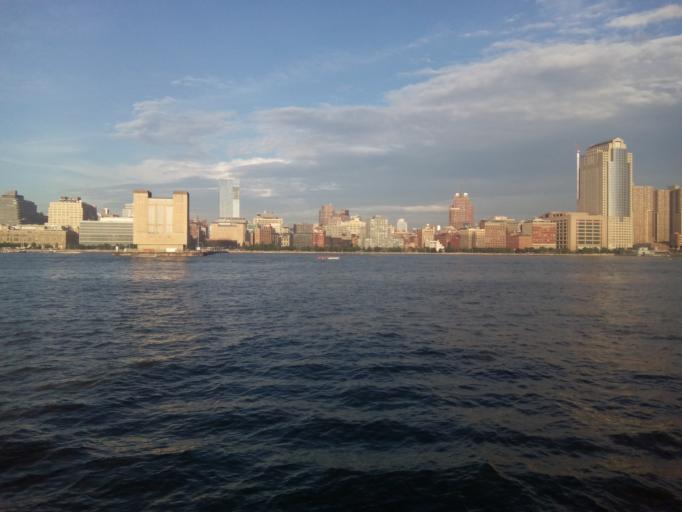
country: US
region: New York
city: New York City
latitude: 40.7267
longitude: -74.0199
